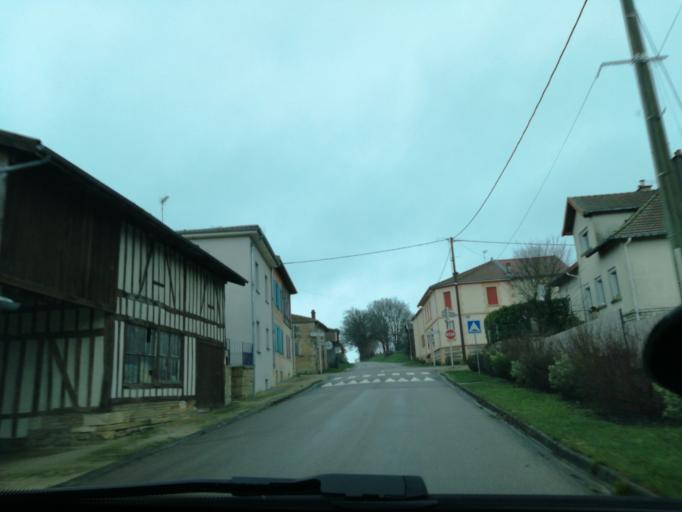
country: FR
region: Lorraine
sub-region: Departement de la Meuse
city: Revigny-sur-Ornain
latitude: 48.8850
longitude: 5.0784
